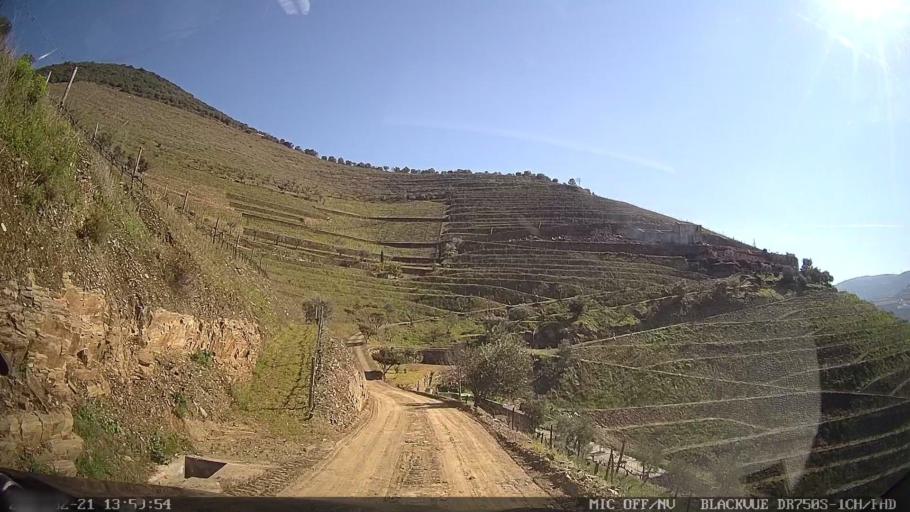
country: PT
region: Viseu
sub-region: Tabuaco
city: Tabuaco
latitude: 41.1760
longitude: -7.5475
